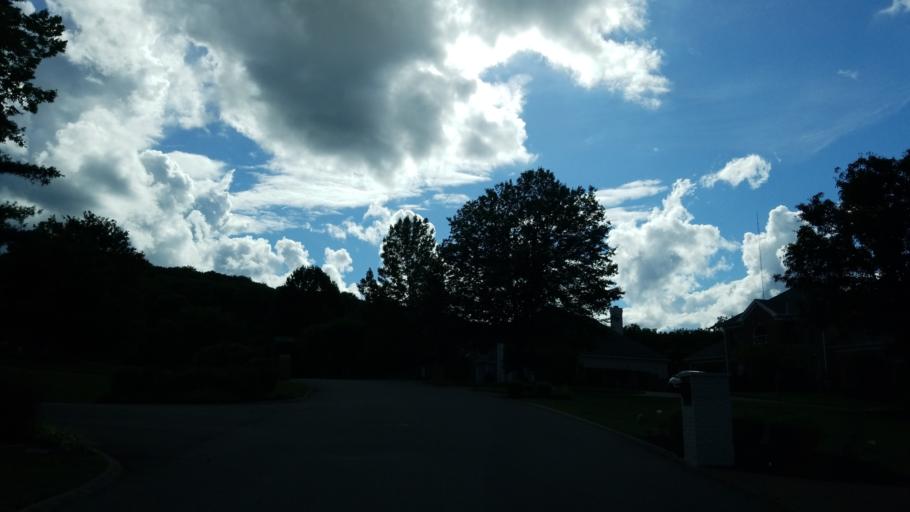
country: US
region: Tennessee
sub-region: Davidson County
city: Forest Hills
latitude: 36.0286
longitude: -86.8325
